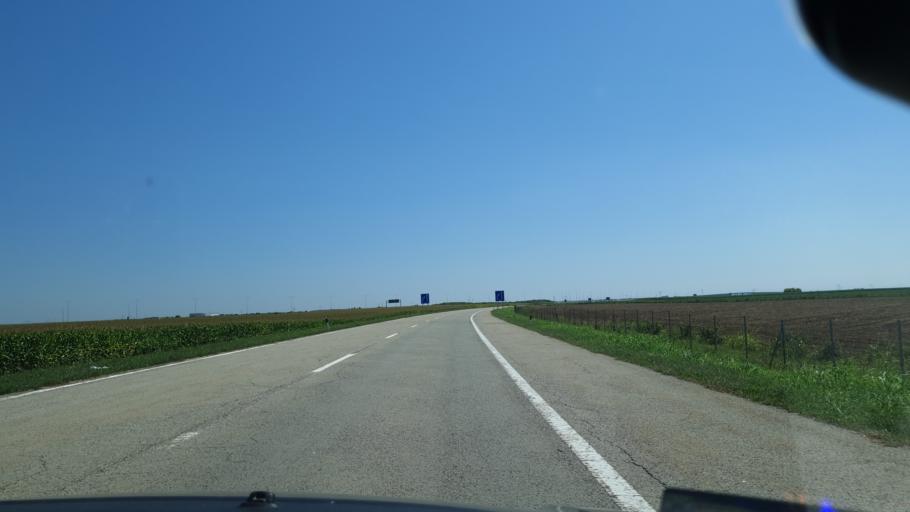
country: RS
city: Krcedin
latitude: 45.0988
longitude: 20.1093
